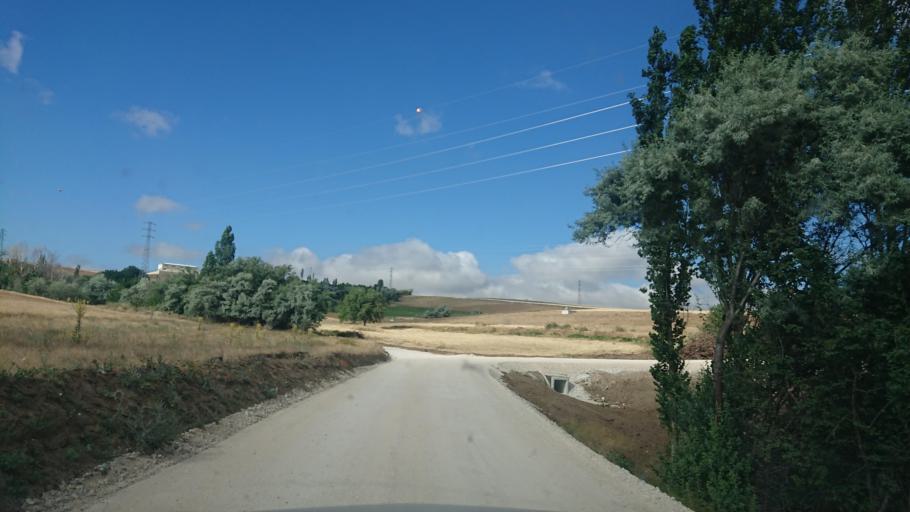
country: TR
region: Aksaray
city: Agacoren
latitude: 38.8585
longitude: 33.9444
